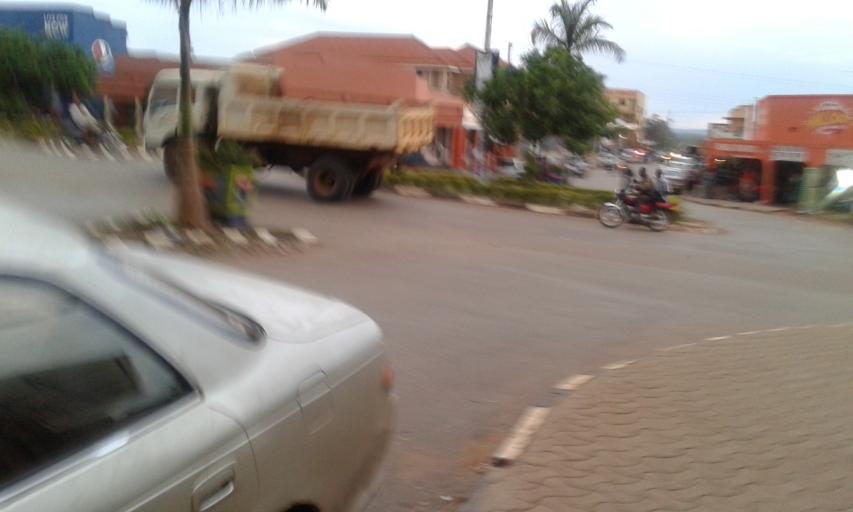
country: UG
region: Eastern Region
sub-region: Mbale District
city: Mbale
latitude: 1.0720
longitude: 34.1799
